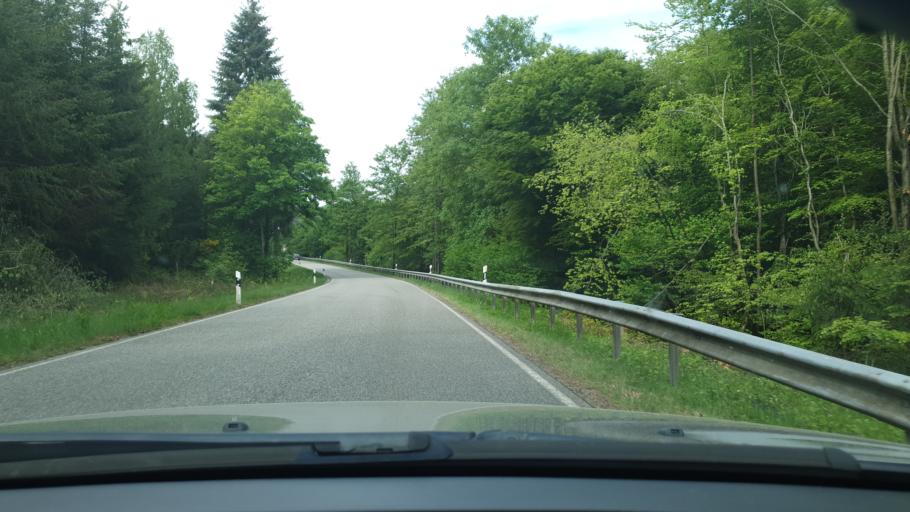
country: DE
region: Rheinland-Pfalz
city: Oberarnbach
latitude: 49.3898
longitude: 7.5659
